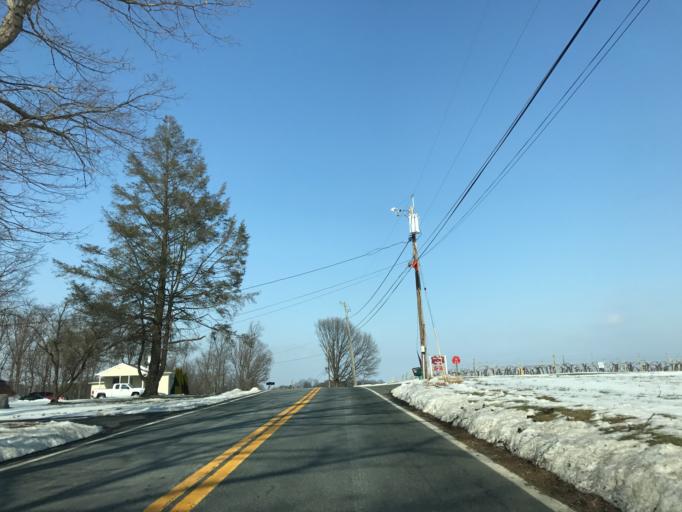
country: US
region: Pennsylvania
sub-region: York County
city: Susquehanna Trails
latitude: 39.7099
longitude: -76.4025
